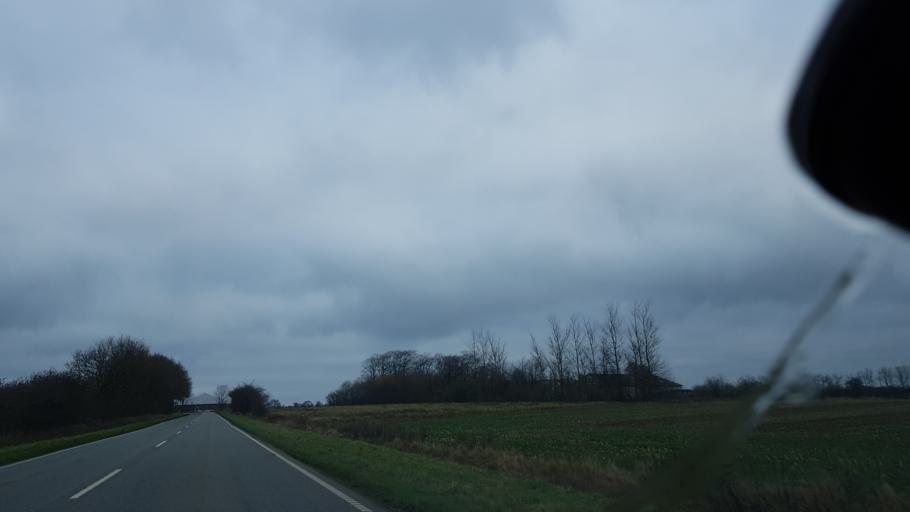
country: DK
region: South Denmark
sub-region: Haderslev Kommune
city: Vojens
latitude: 55.2388
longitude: 9.2177
